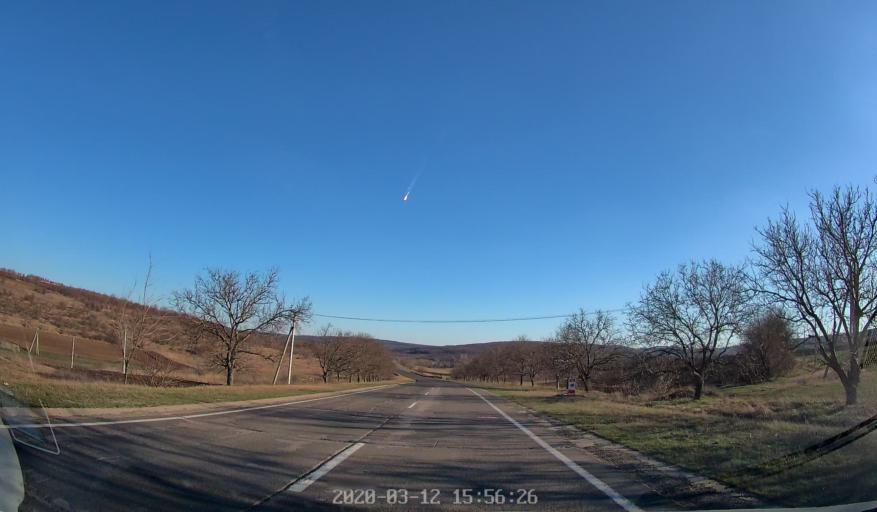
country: MD
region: Chisinau
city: Vadul lui Voda
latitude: 47.0631
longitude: 29.0331
